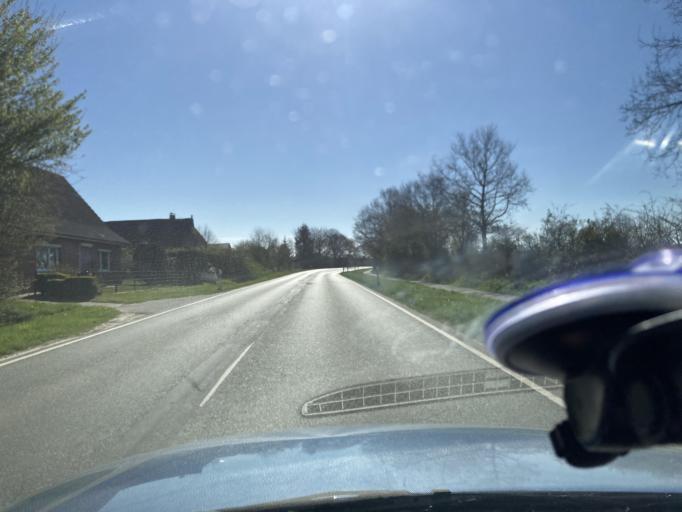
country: DE
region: Schleswig-Holstein
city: Nordhastedt
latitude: 54.1823
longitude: 9.1729
